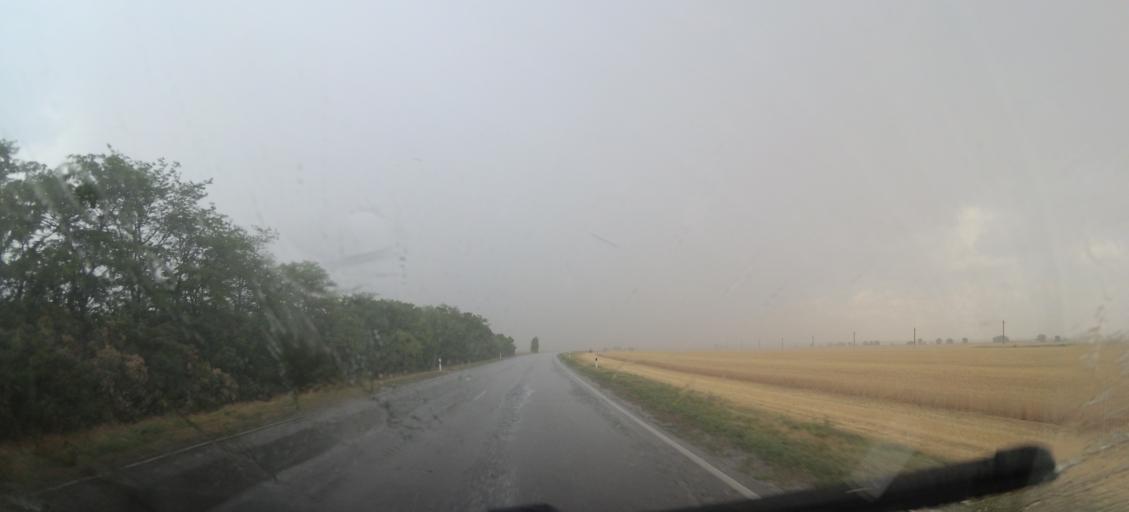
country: RU
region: Rostov
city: Proletarsk
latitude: 46.6704
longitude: 41.6928
